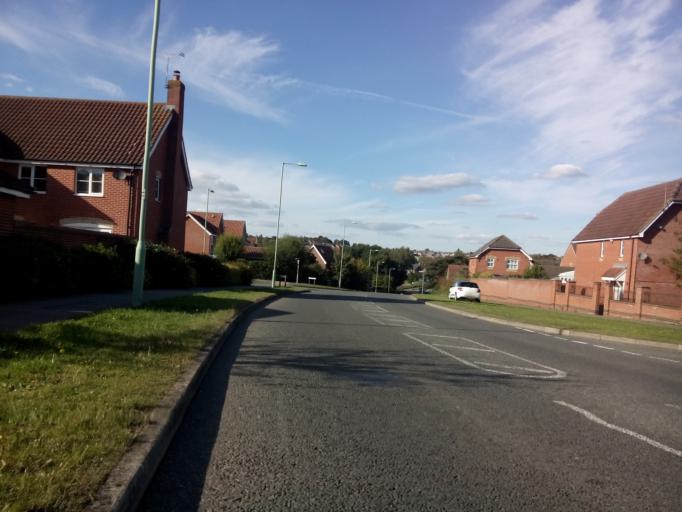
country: GB
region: England
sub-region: Suffolk
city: Ipswich
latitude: 52.0338
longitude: 1.1185
